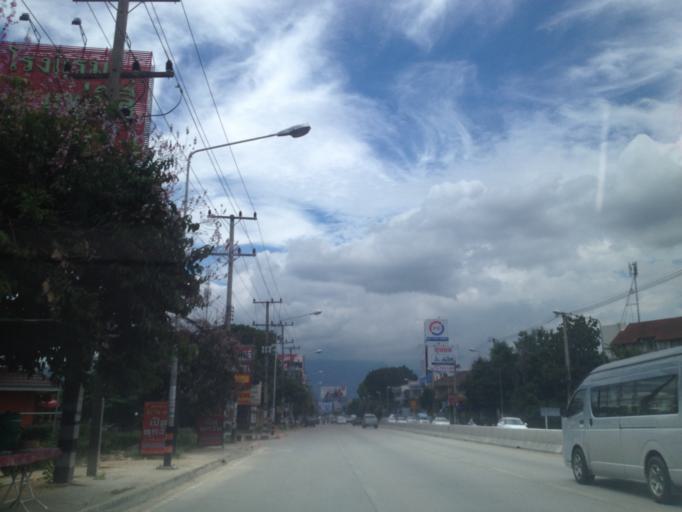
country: TH
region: Chiang Mai
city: Chiang Mai
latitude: 18.7614
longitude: 98.9957
